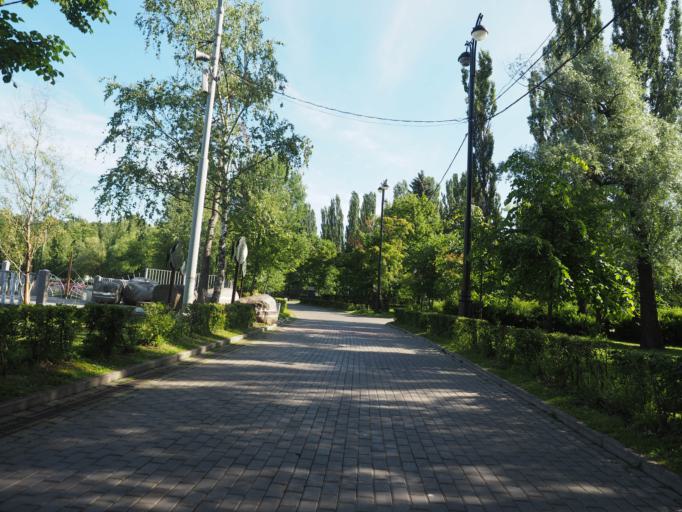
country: RU
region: Moscow
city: Ryazanskiy
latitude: 55.7714
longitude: 37.7524
